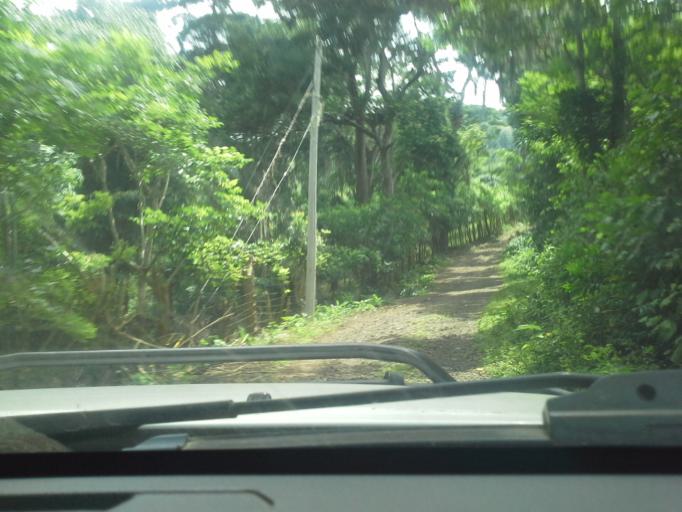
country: NI
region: Boaco
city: San Jose de los Remates
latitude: 12.6954
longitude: -85.7426
